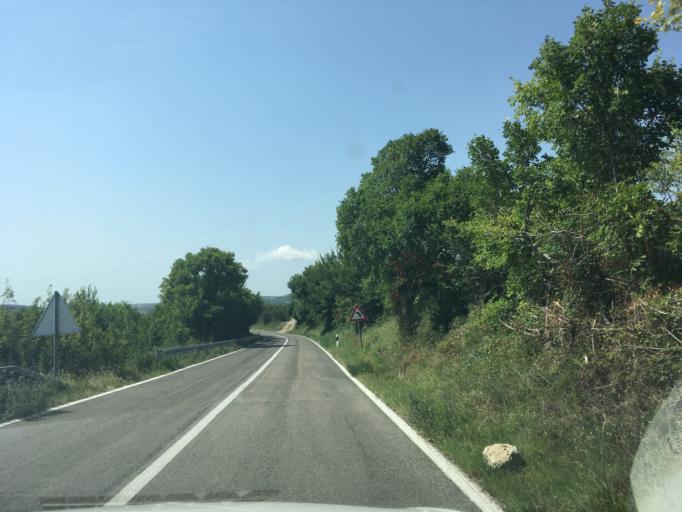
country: HR
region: Sibensko-Kniniska
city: Zaton
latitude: 43.9308
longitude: 15.8293
